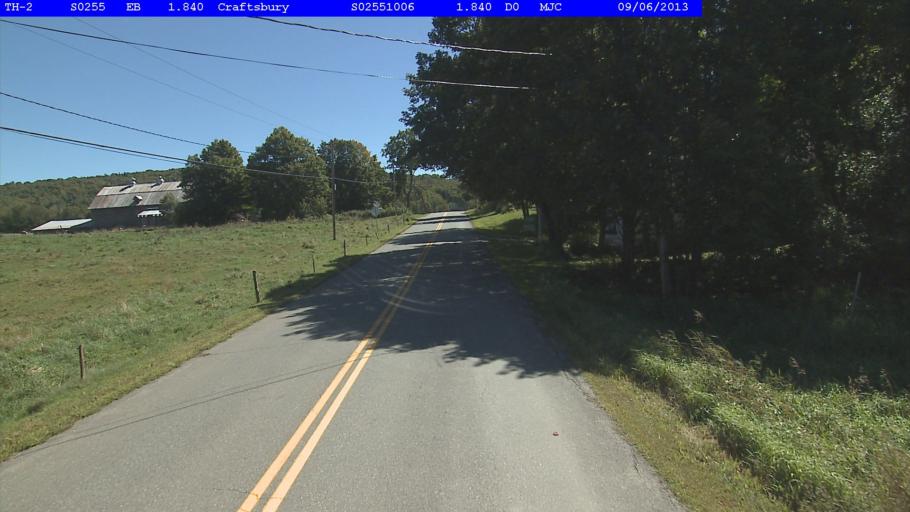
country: US
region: Vermont
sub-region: Caledonia County
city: Hardwick
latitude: 44.6408
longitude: -72.3405
